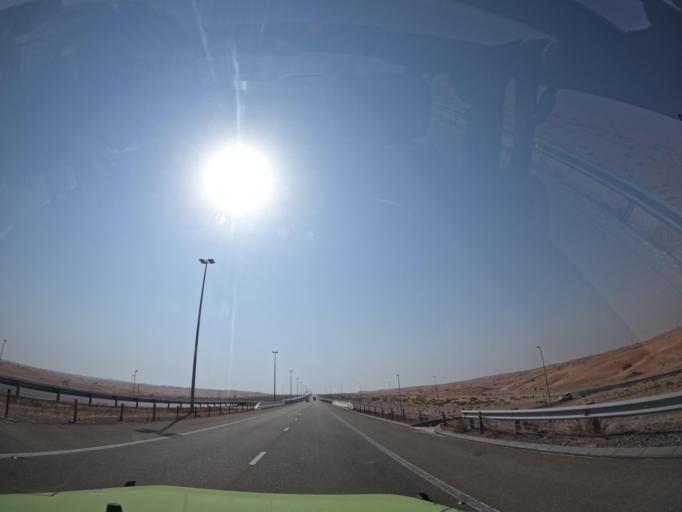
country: OM
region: Al Buraimi
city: Al Buraymi
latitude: 24.4390
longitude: 55.6670
